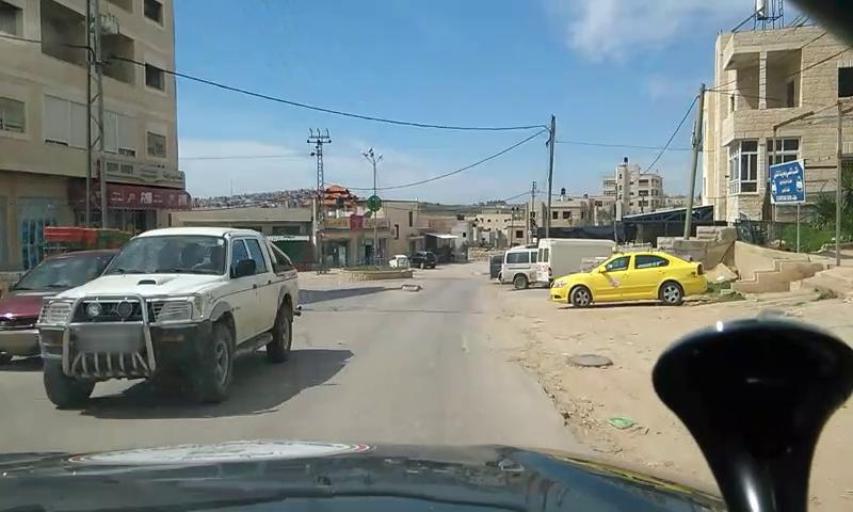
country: PS
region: West Bank
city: Al Jib
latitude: 31.8527
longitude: 35.1843
